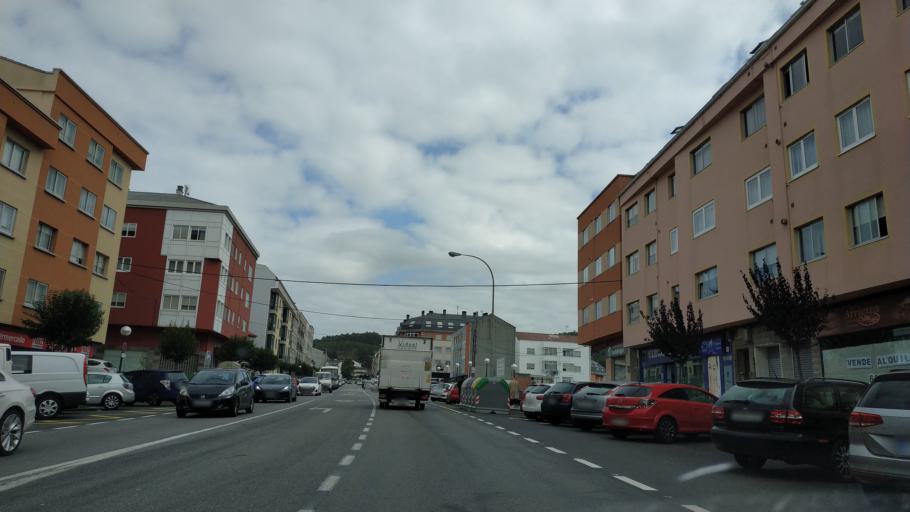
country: ES
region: Galicia
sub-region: Provincia da Coruna
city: Arteixo
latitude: 43.3169
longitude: -8.4820
